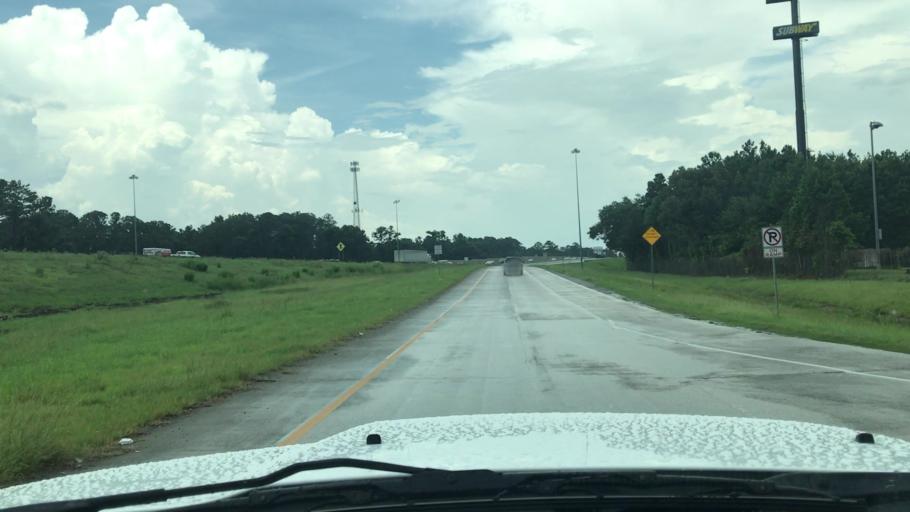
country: US
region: Georgia
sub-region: Glynn County
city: Brunswick
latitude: 31.1379
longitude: -81.5738
